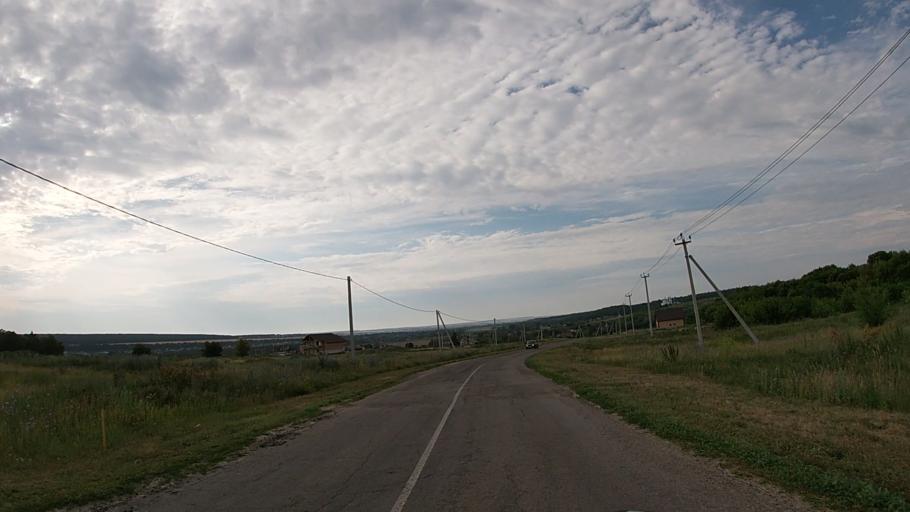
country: RU
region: Belgorod
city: Severnyy
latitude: 50.7172
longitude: 36.5900
